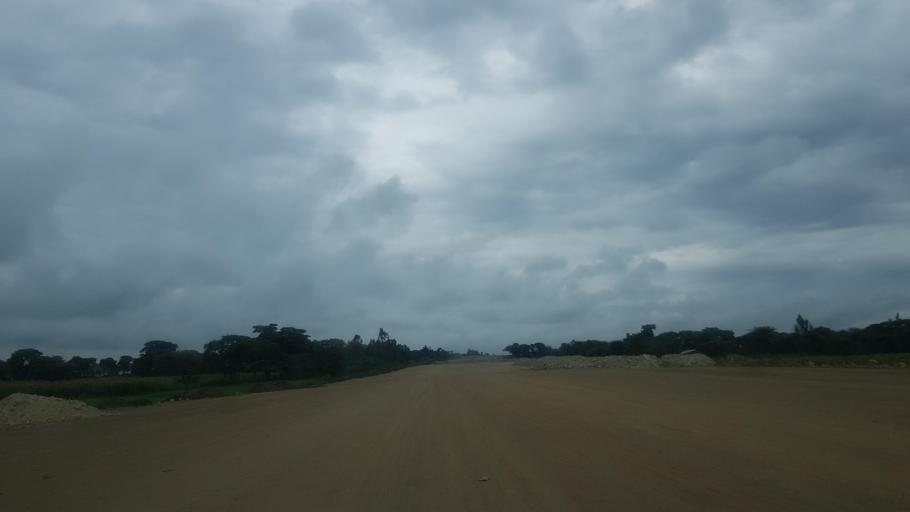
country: ET
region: Oromiya
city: Shashemene
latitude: 7.3440
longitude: 38.6368
